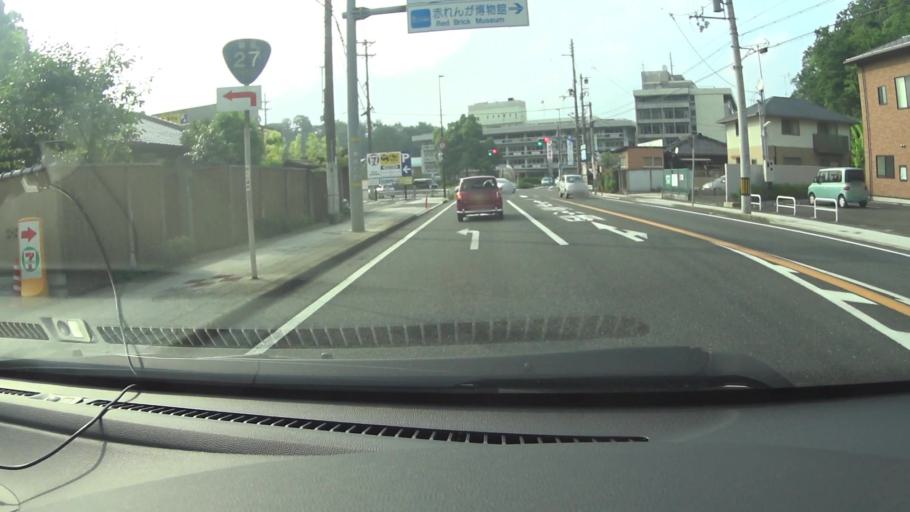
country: JP
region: Kyoto
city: Maizuru
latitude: 35.4734
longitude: 135.3871
